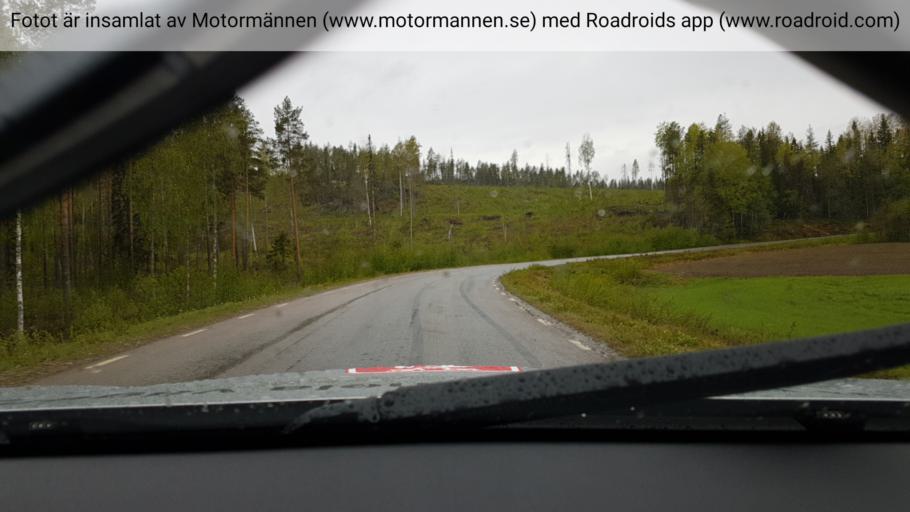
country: SE
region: Vaesterbotten
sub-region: Vannas Kommun
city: Vaennaes
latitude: 63.8898
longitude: 19.7115
